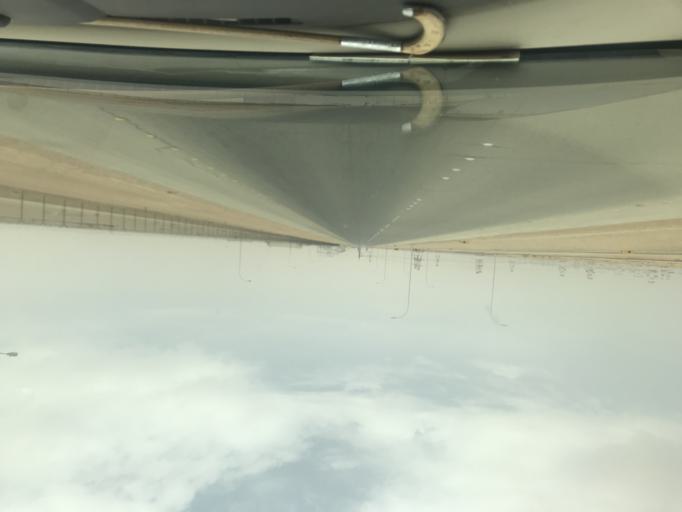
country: SA
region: Ar Riyad
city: Riyadh
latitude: 24.9688
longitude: 46.6645
